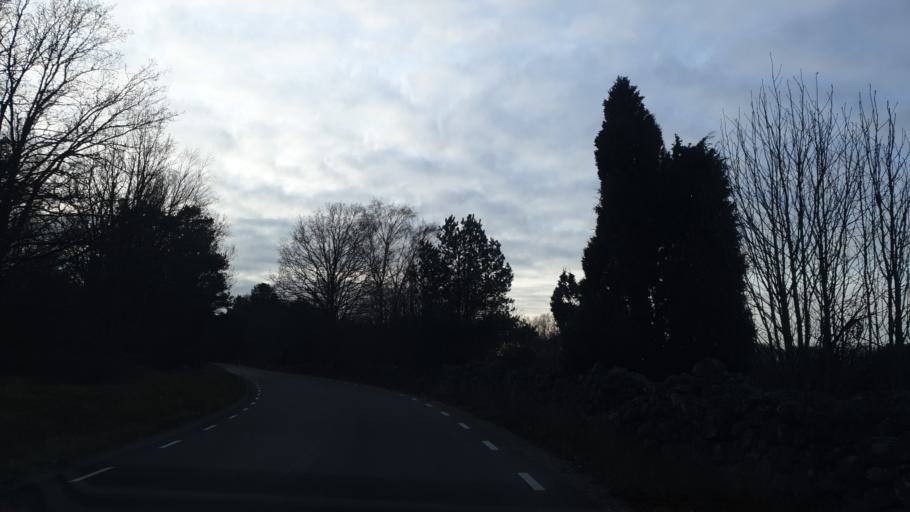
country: SE
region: Blekinge
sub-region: Karlskrona Kommun
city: Jaemjoe
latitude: 56.2243
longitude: 15.9890
